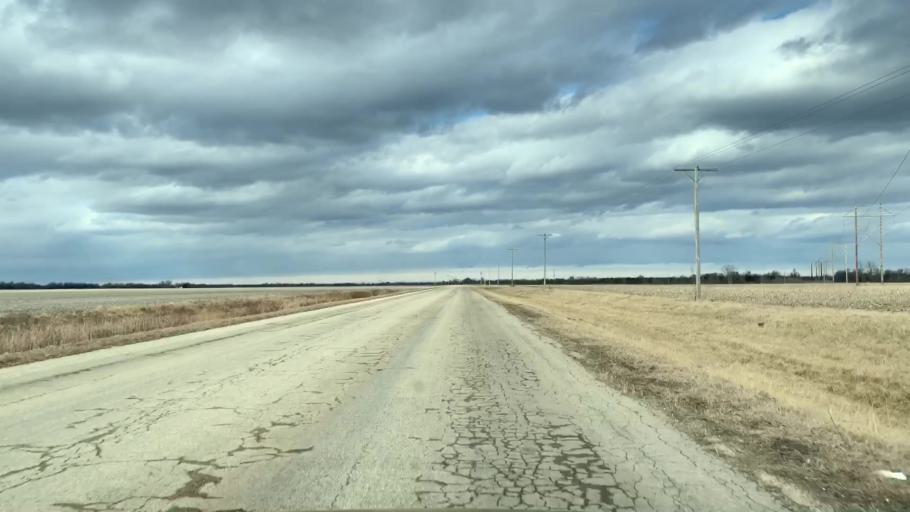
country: US
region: Kansas
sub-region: Allen County
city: Humboldt
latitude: 37.7709
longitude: -95.4706
